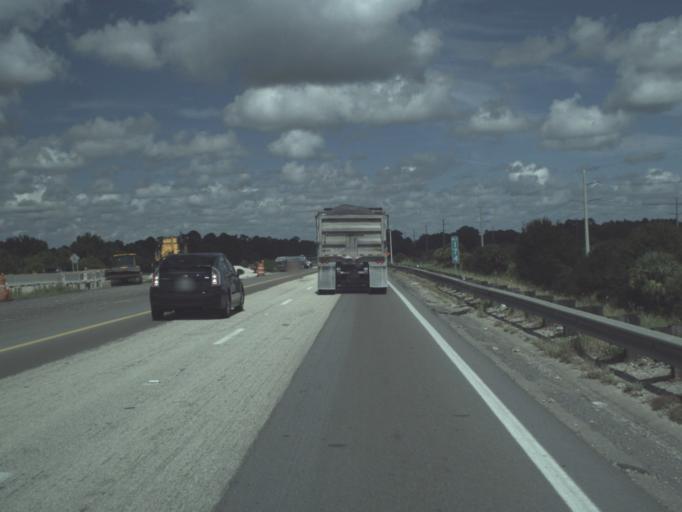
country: US
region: Florida
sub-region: Charlotte County
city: Port Charlotte
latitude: 27.0605
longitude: -82.0853
